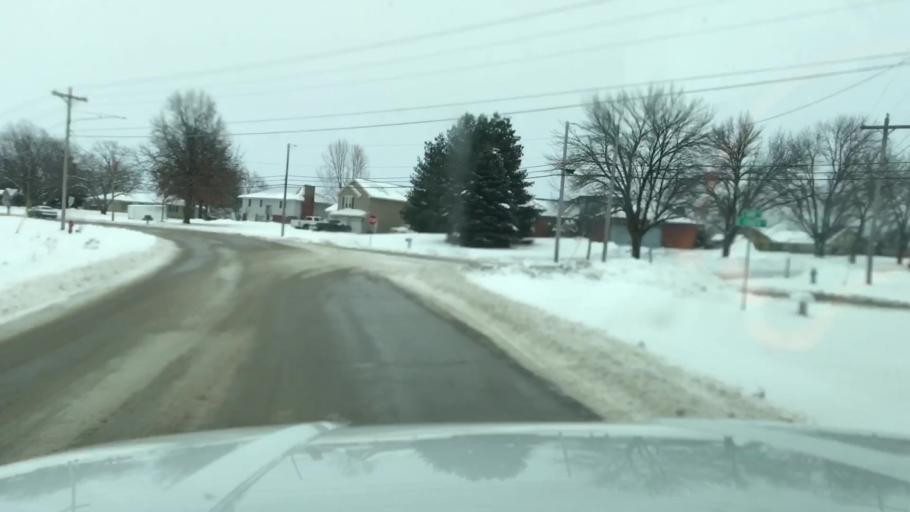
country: US
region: Missouri
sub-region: Clinton County
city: Cameron
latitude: 39.7427
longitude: -94.2259
